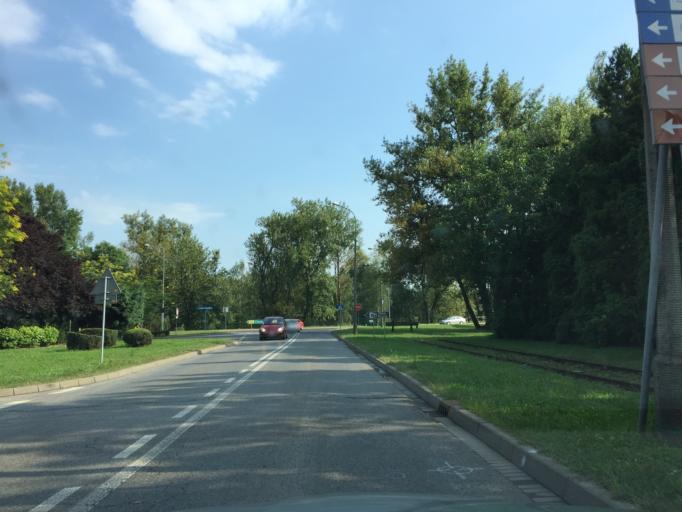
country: PL
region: Lesser Poland Voivodeship
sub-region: Powiat oswiecimski
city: Oswiecim
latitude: 50.0245
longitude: 19.2023
